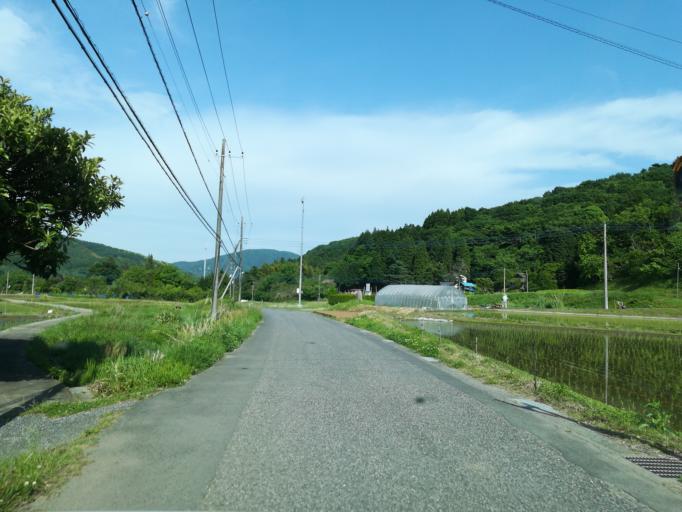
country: JP
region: Ibaraki
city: Tsukuba
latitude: 36.1883
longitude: 140.1532
